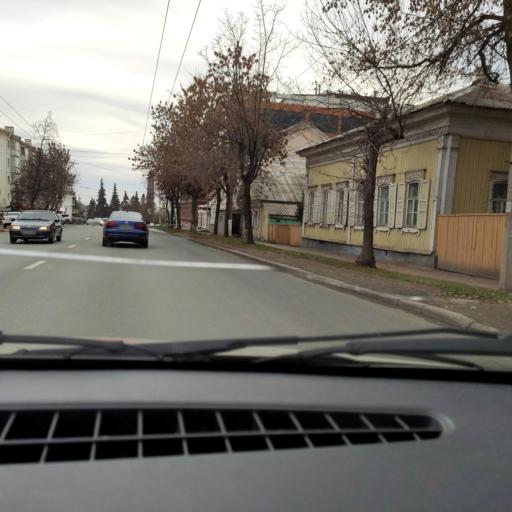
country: RU
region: Bashkortostan
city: Ufa
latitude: 54.7147
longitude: 55.9624
